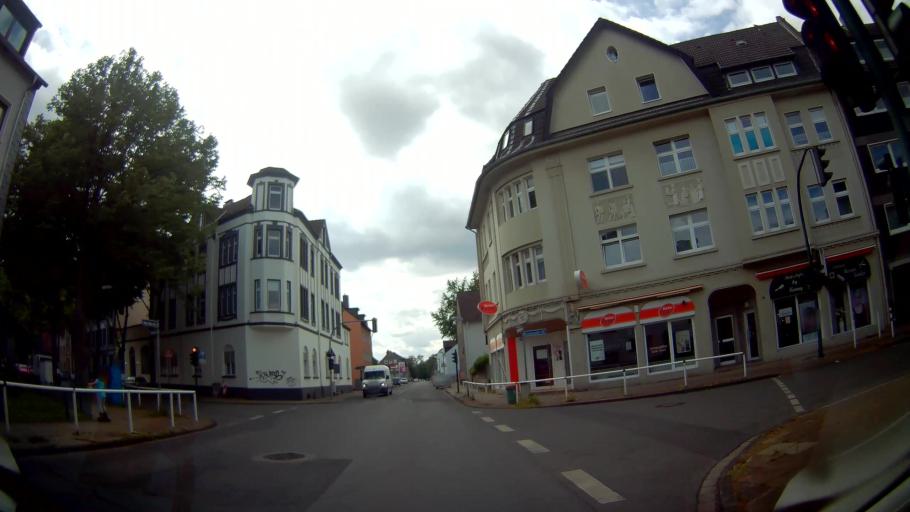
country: DE
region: North Rhine-Westphalia
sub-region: Regierungsbezirk Munster
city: Bottrop
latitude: 51.4919
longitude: 6.9413
